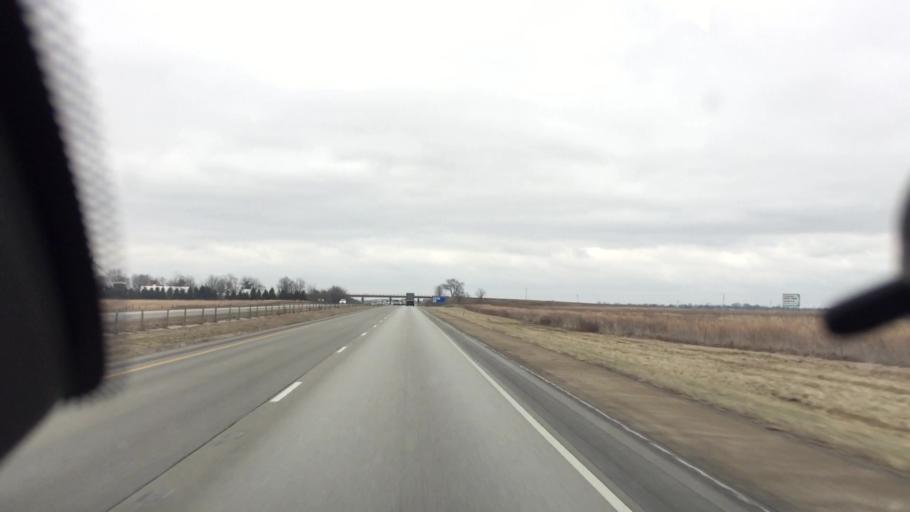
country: US
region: Illinois
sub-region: Vermilion County
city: Oakwood
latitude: 40.1260
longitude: -87.8173
